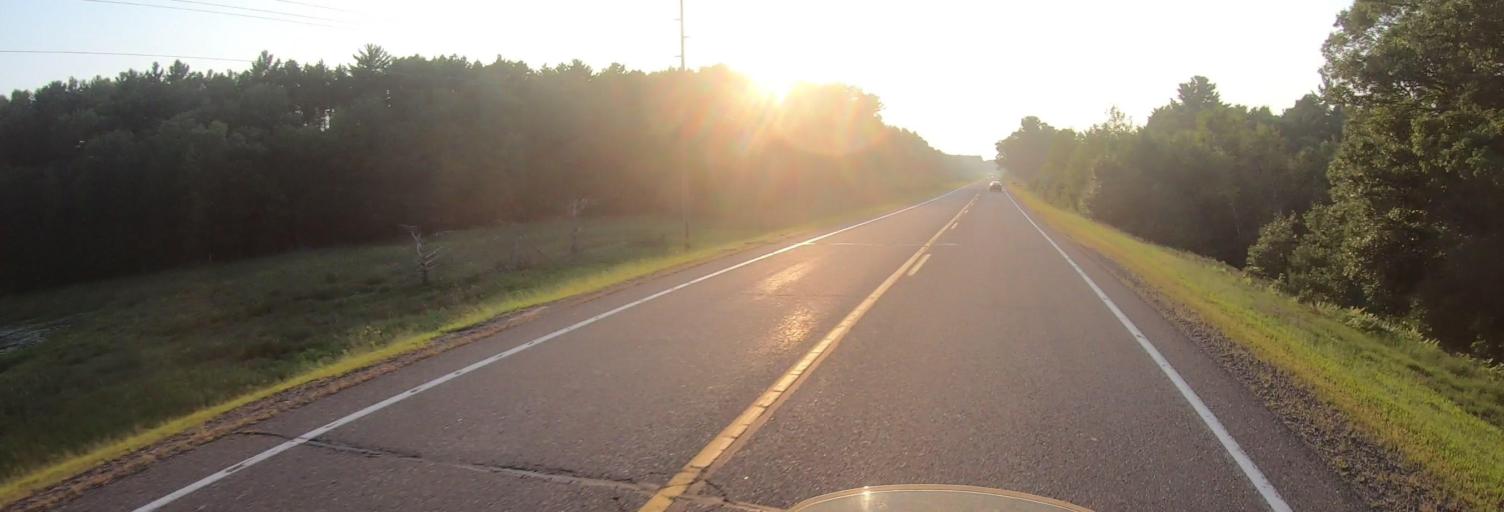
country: US
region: Wisconsin
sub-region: Burnett County
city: Siren
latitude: 45.8101
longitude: -92.2222
